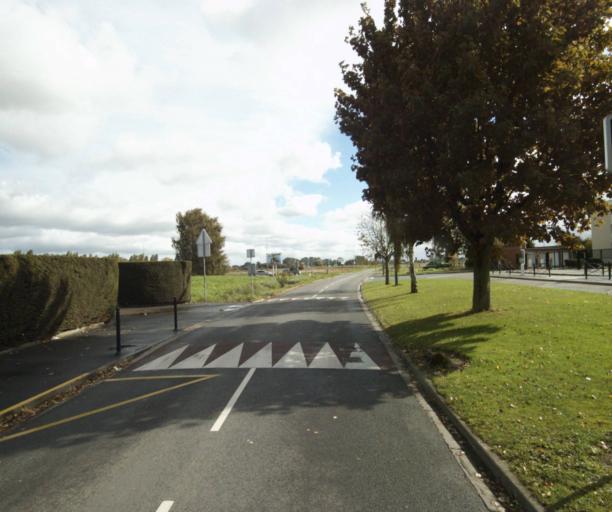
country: FR
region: Nord-Pas-de-Calais
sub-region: Departement du Nord
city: Houplines
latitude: 50.6885
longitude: 2.9190
